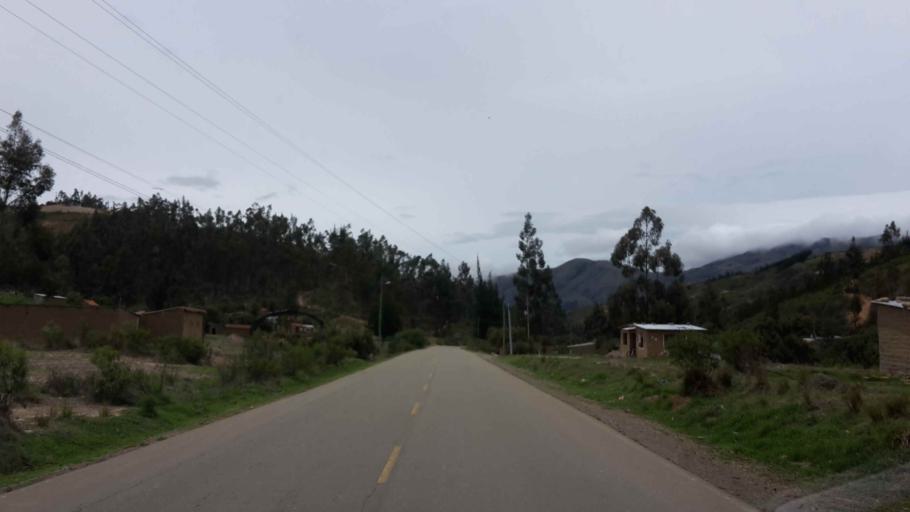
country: BO
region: Cochabamba
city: Totora
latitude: -17.6815
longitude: -65.2157
